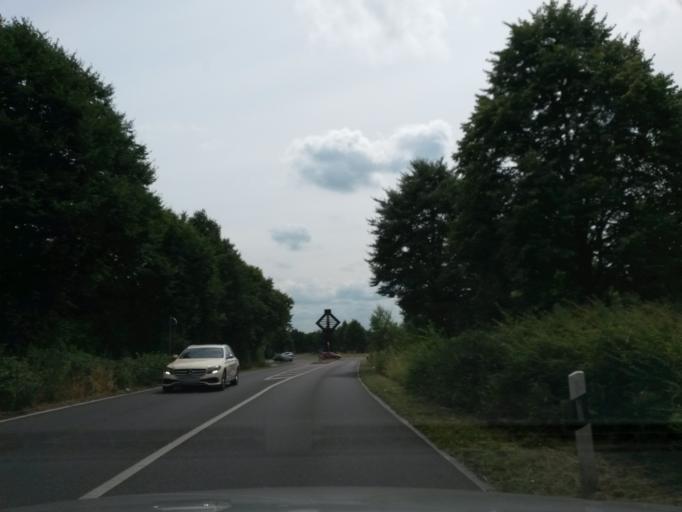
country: DE
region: North Rhine-Westphalia
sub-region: Regierungsbezirk Dusseldorf
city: Nettetal
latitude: 51.3365
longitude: 6.2731
